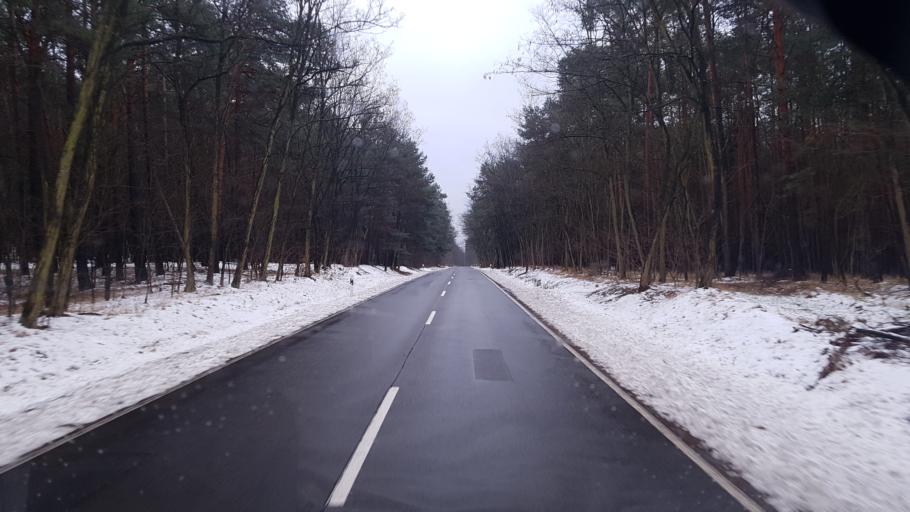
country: DE
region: Brandenburg
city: Schenkendobern
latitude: 51.9244
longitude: 14.6209
